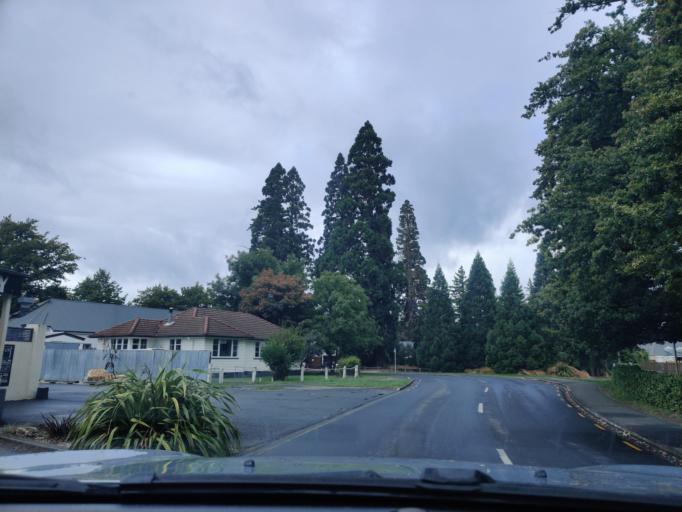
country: NZ
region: Canterbury
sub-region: Hurunui District
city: Amberley
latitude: -42.5216
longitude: 172.8285
